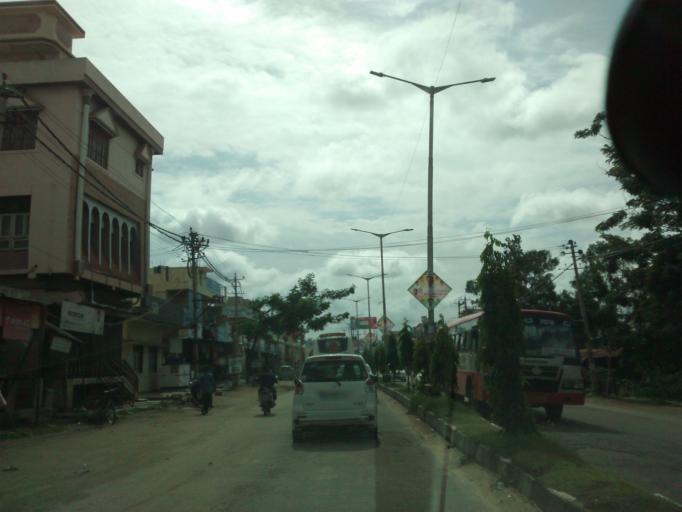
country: IN
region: Karnataka
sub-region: Tumkur
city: Koratagere
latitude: 13.5202
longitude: 77.2370
